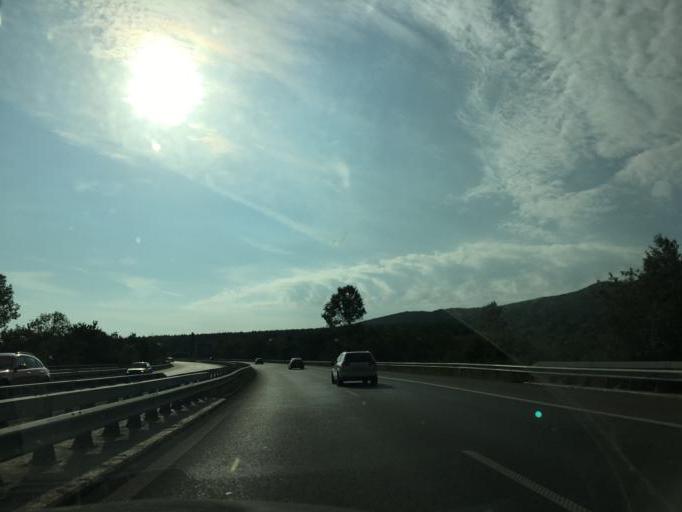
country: BG
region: Sofiya
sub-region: Obshtina Elin Pelin
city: Elin Pelin
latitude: 42.6065
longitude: 23.5483
